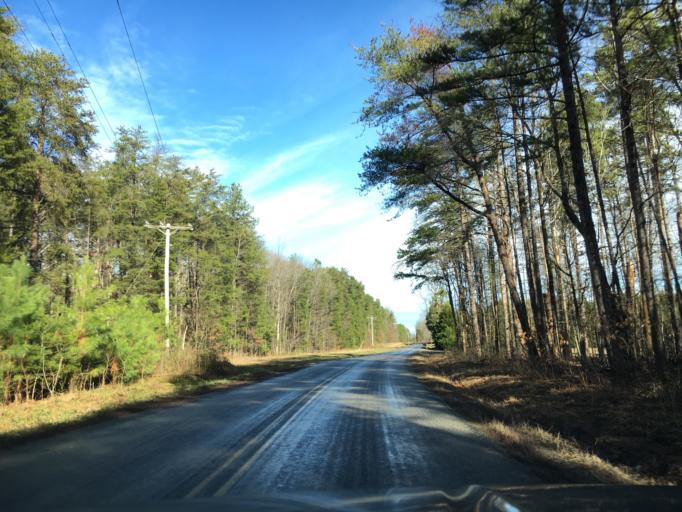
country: US
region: Virginia
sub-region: Nottoway County
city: Crewe
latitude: 37.3427
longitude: -78.1598
